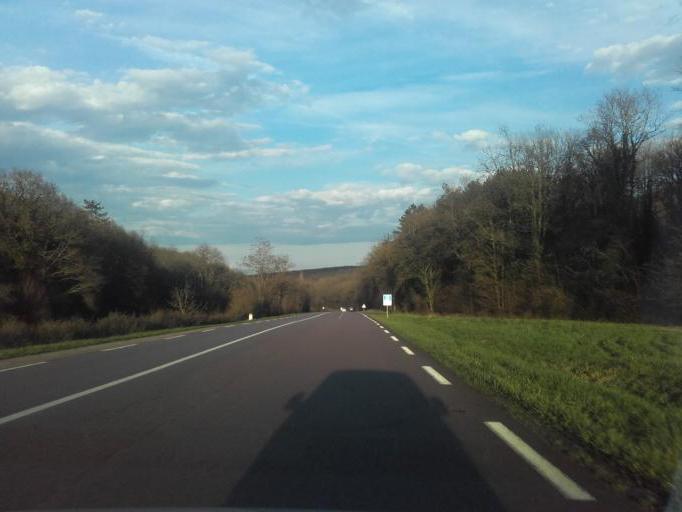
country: FR
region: Bourgogne
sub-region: Departement de la Cote-d'Or
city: Nolay
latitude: 46.9392
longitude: 4.6885
